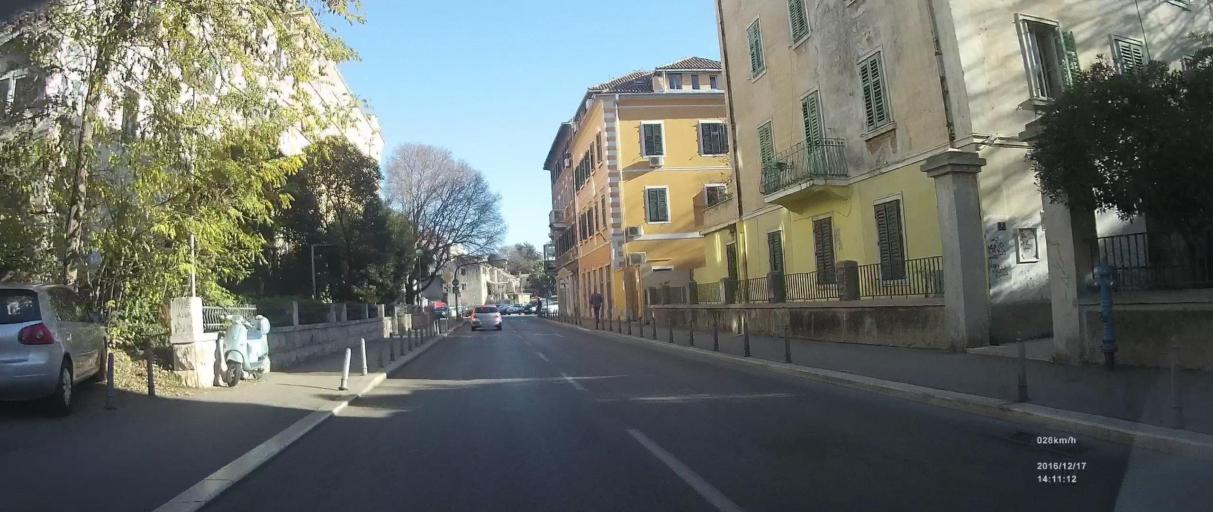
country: HR
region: Splitsko-Dalmatinska
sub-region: Grad Split
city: Split
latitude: 43.5131
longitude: 16.4368
